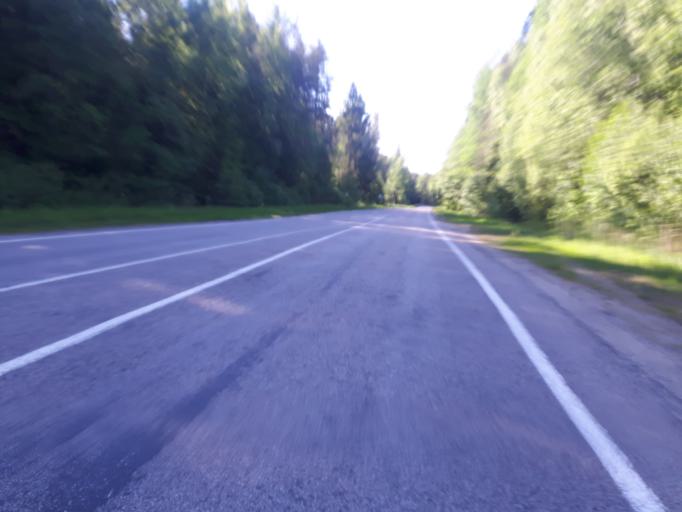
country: EE
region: Harju
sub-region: Loksa linn
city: Loksa
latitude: 59.5645
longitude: 25.9767
